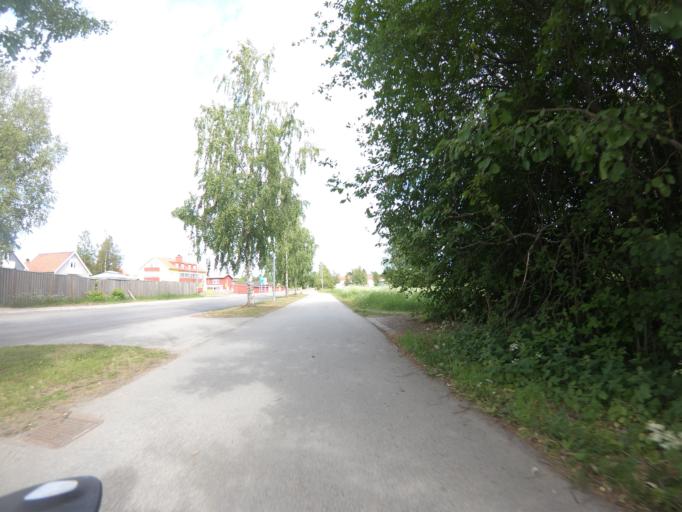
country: SE
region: Vaesterbotten
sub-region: Umea Kommun
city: Umea
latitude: 63.8143
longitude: 20.2669
